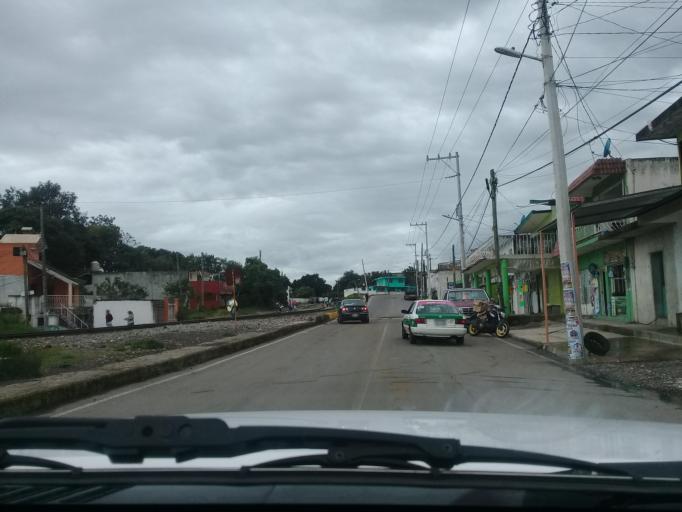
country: MX
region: Veracruz
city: Rafael Lucio
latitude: 19.5964
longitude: -96.9891
